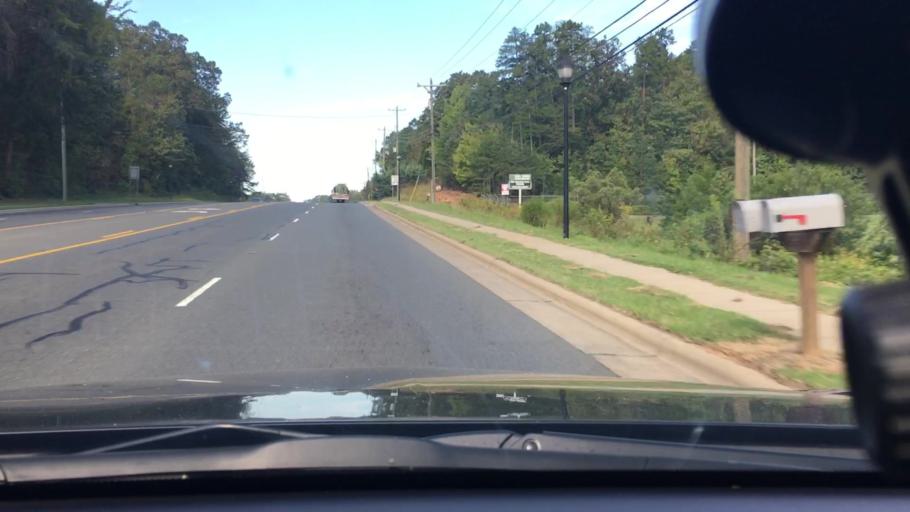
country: US
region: North Carolina
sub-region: Stanly County
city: Locust
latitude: 35.2612
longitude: -80.4083
